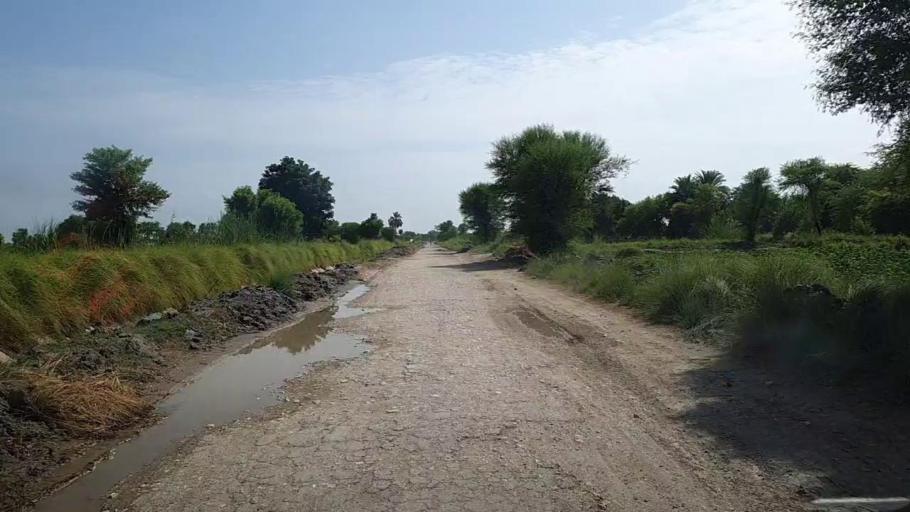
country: PK
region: Sindh
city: Bhiria
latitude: 26.8838
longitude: 68.2349
